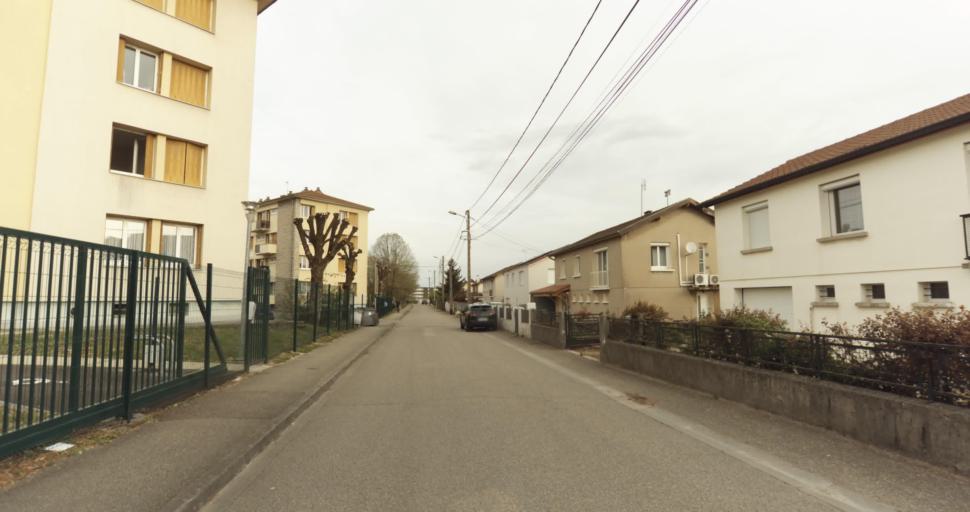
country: FR
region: Rhone-Alpes
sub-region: Departement de l'Ain
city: Amberieu-en-Bugey
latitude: 45.9585
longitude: 5.3400
